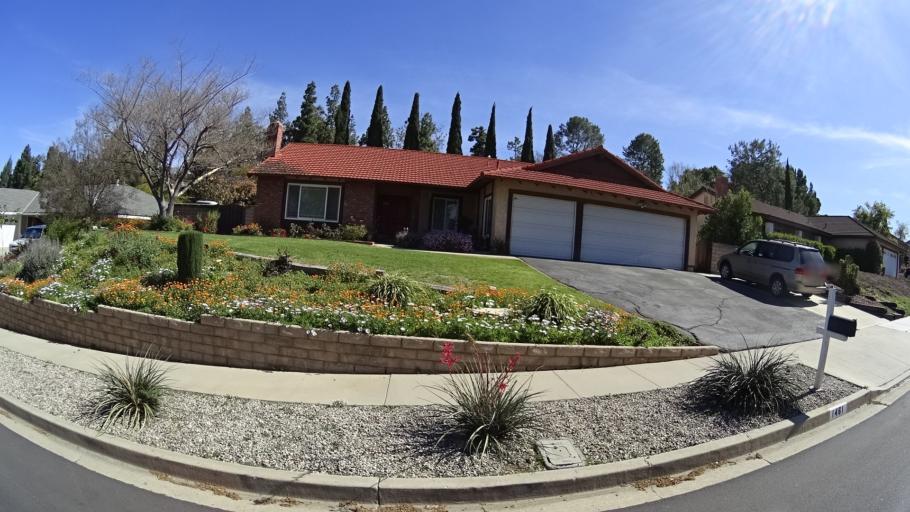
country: US
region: California
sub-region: Ventura County
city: Thousand Oaks
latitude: 34.2181
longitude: -118.8535
